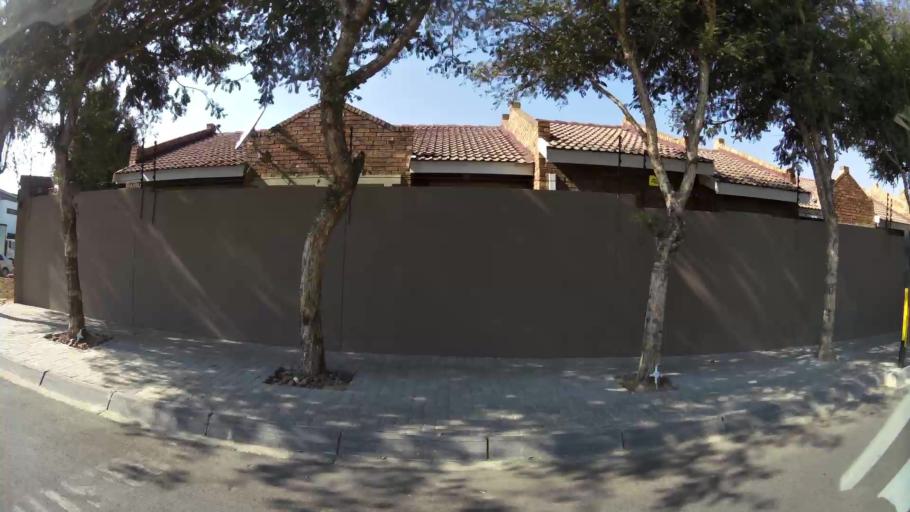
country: ZA
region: Gauteng
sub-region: City of Johannesburg Metropolitan Municipality
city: Modderfontein
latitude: -26.1188
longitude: 28.1544
